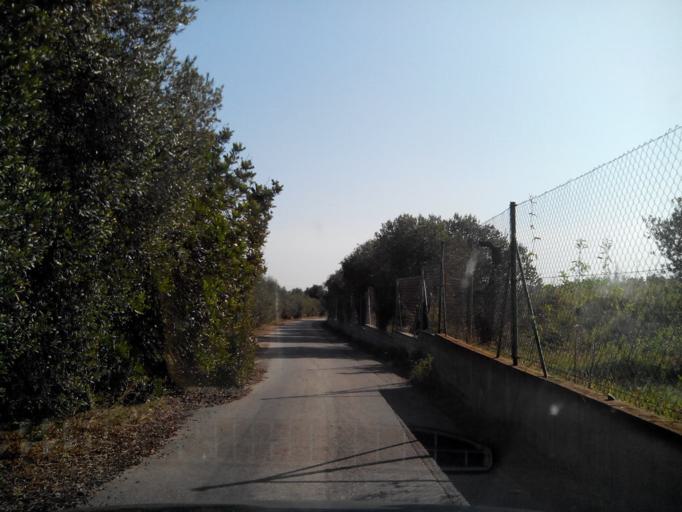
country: ES
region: Catalonia
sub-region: Provincia de Tarragona
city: La Selva
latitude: 41.2133
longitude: 1.1640
